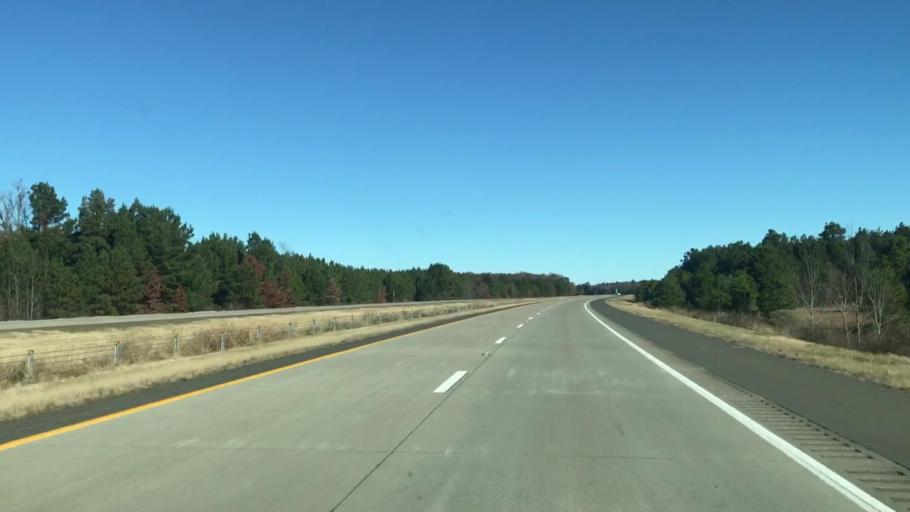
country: US
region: Texas
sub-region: Cass County
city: Queen City
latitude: 33.2019
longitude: -93.8769
